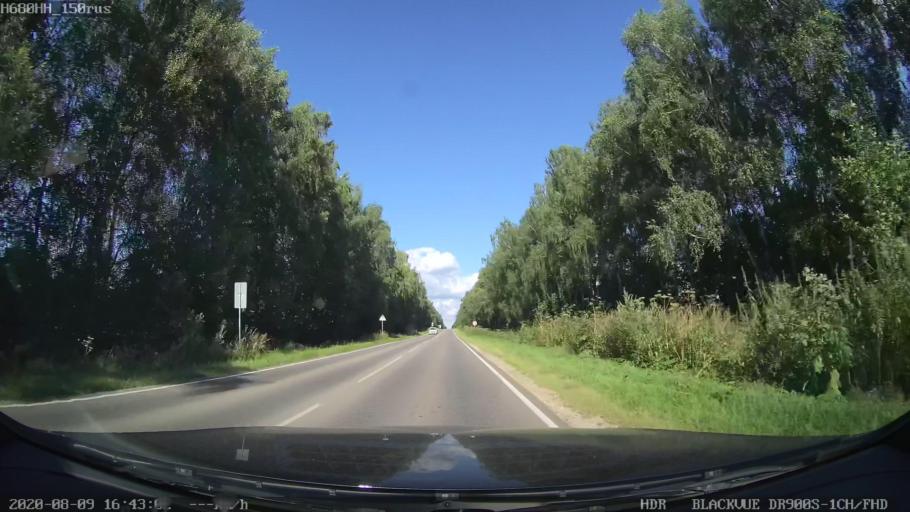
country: RU
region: Tula
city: Zaokskiy
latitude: 54.7320
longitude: 37.3348
